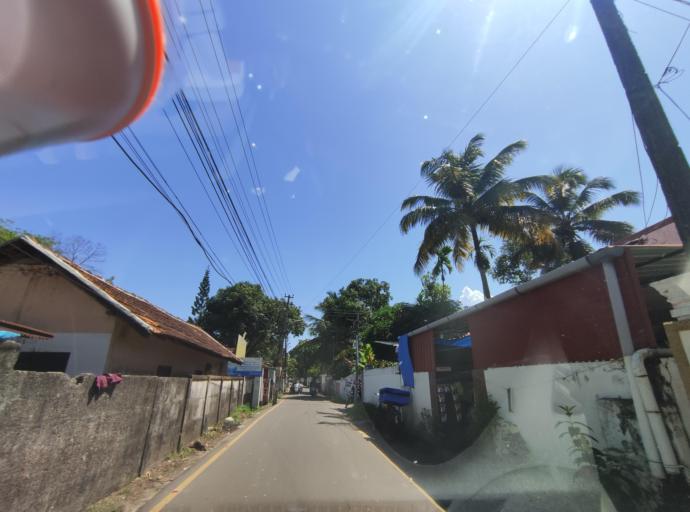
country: IN
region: Kerala
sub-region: Alappuzha
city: Alleppey
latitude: 9.4772
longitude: 76.3309
